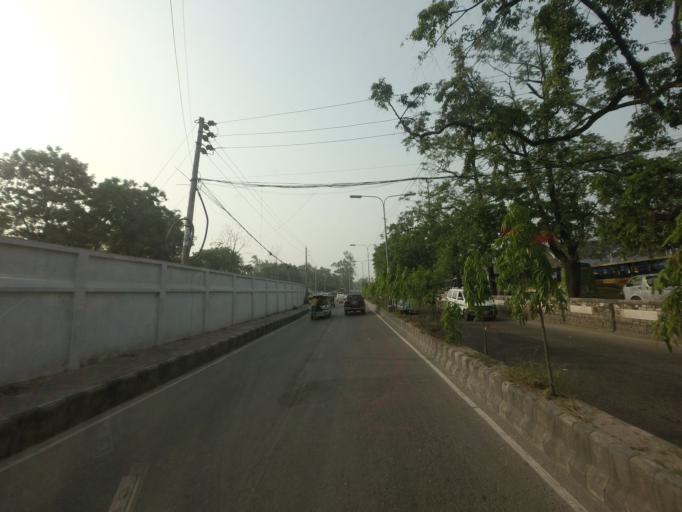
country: BD
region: Dhaka
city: Azimpur
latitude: 23.7713
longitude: 90.3825
